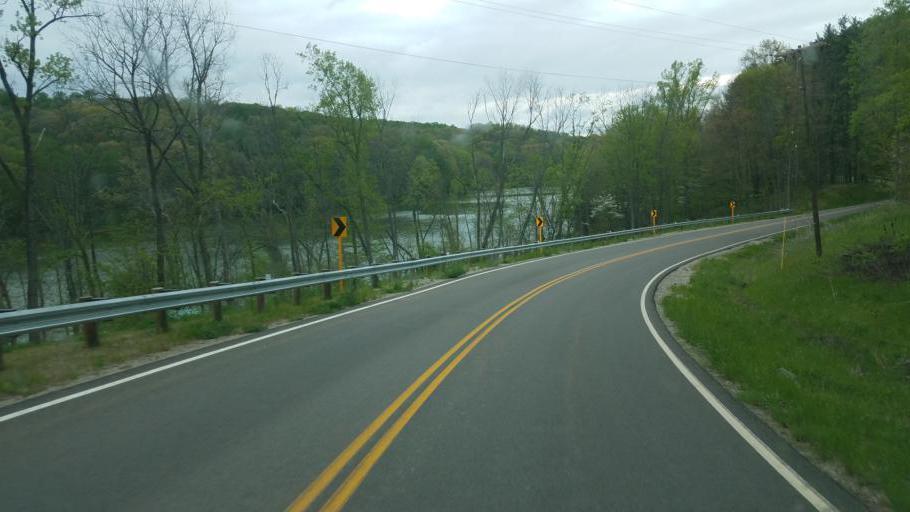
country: US
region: Ohio
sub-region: Ashland County
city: Loudonville
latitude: 40.6262
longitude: -82.3215
